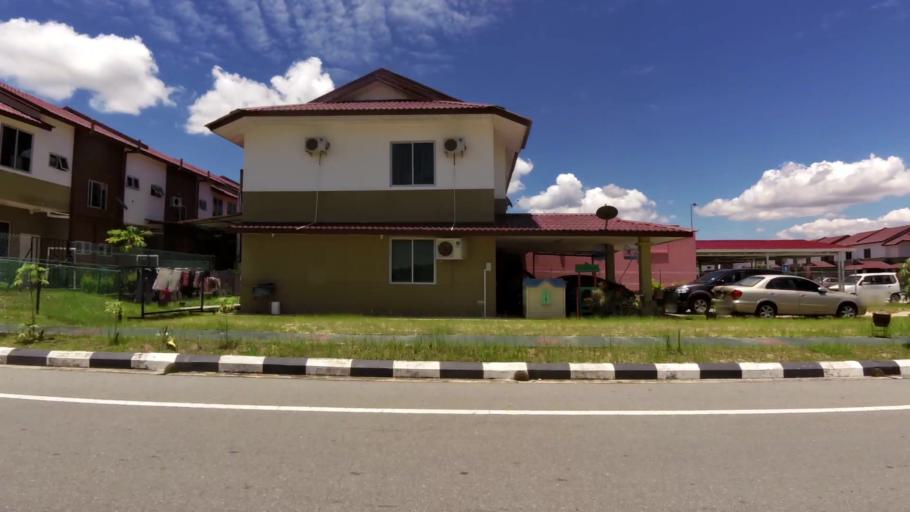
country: BN
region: Brunei and Muara
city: Bandar Seri Begawan
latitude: 5.0075
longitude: 115.0075
